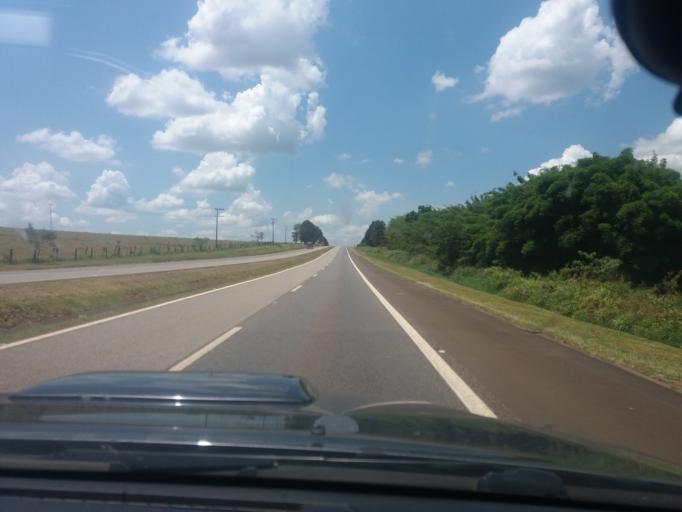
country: BR
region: Sao Paulo
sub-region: Itapetininga
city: Itapetininga
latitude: -23.5143
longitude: -47.9676
